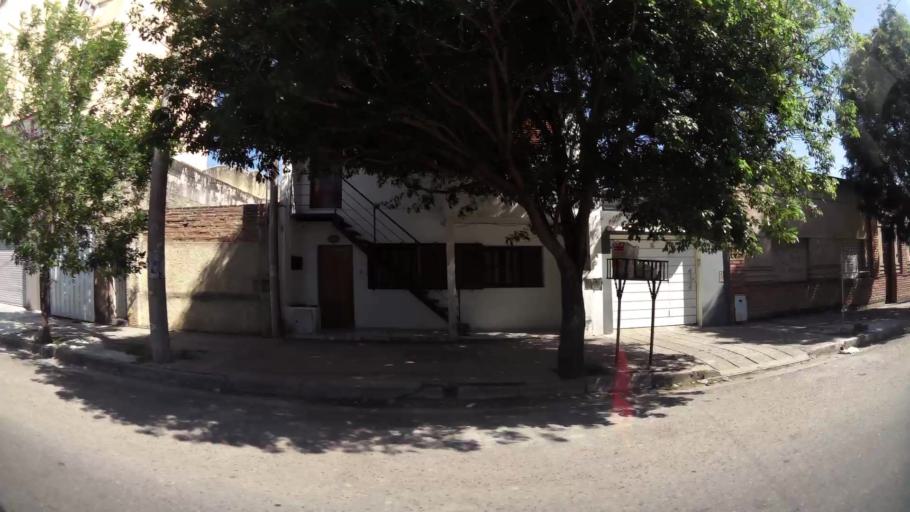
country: AR
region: Cordoba
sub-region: Departamento de Capital
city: Cordoba
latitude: -31.4012
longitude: -64.1702
